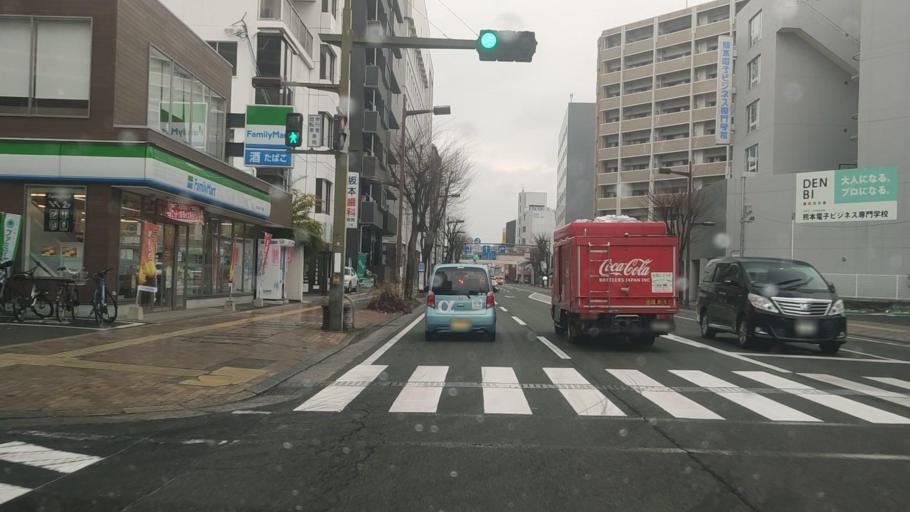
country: JP
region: Kumamoto
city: Kumamoto
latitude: 32.7983
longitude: 130.7162
